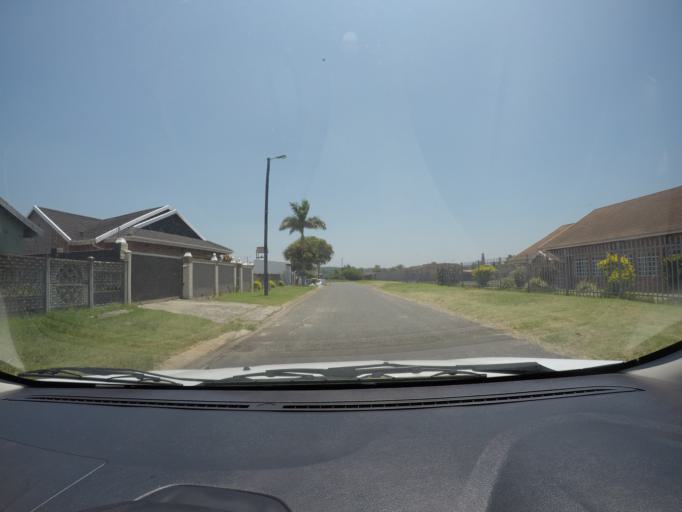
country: ZA
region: KwaZulu-Natal
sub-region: uThungulu District Municipality
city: eSikhawini
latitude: -28.8730
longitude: 31.9053
